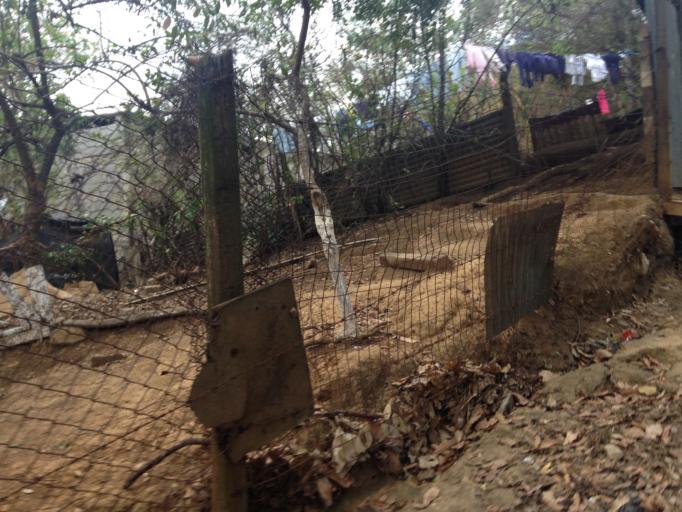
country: GT
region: Guatemala
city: Mixco
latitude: 14.5997
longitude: -90.6034
